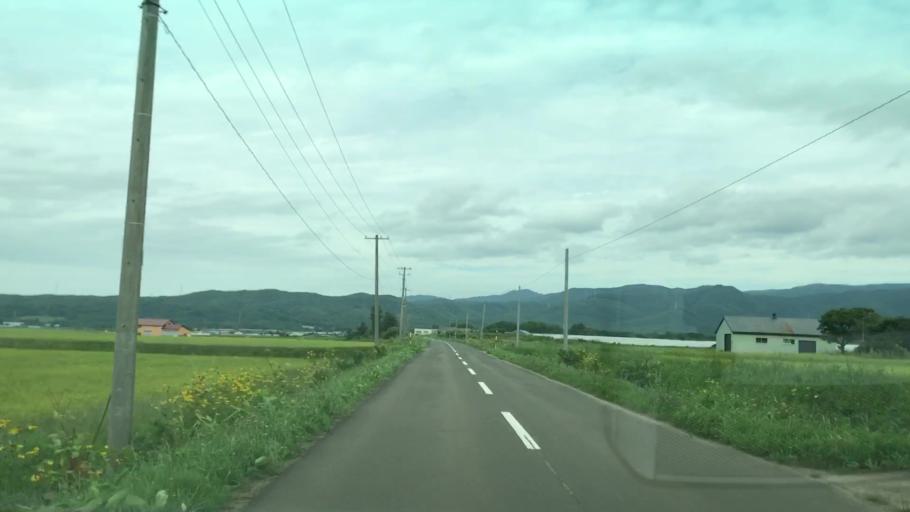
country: JP
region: Hokkaido
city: Iwanai
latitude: 43.0214
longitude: 140.5733
